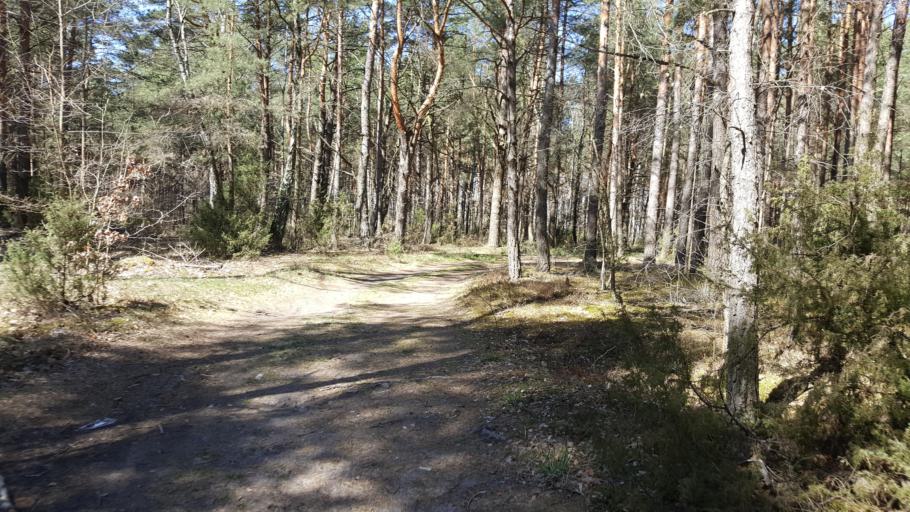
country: BY
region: Brest
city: Zhabinka
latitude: 52.2408
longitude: 23.9531
